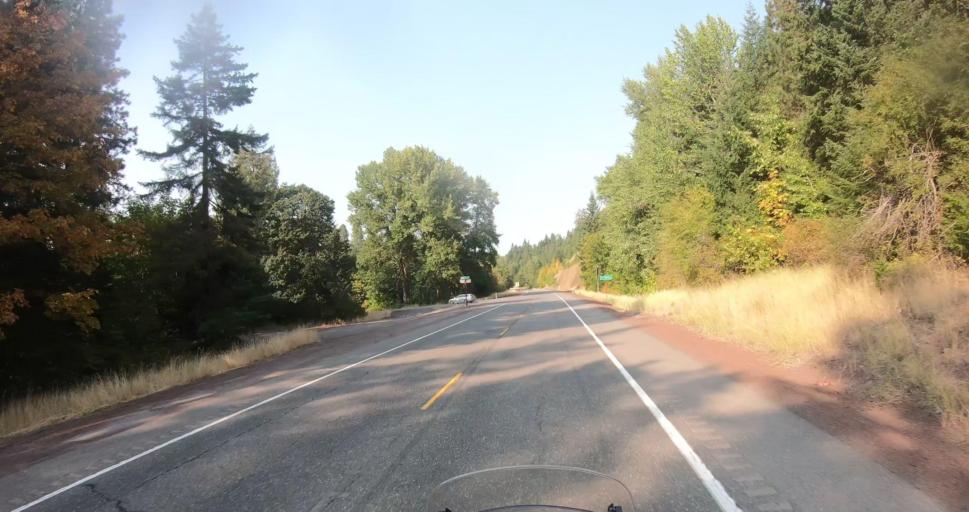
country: US
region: Oregon
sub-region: Hood River County
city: Odell
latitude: 45.4967
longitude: -121.5627
